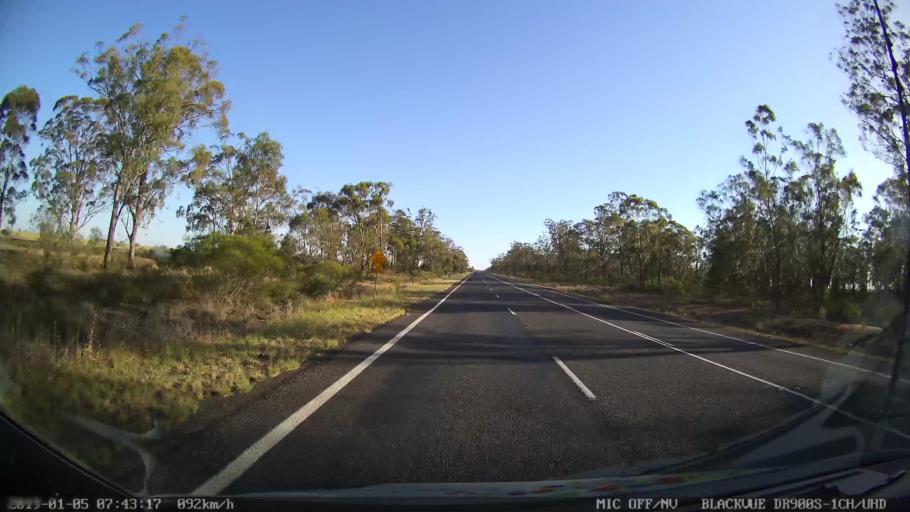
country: AU
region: New South Wales
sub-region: Gilgandra
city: Gilgandra
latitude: -31.8870
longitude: 148.6328
